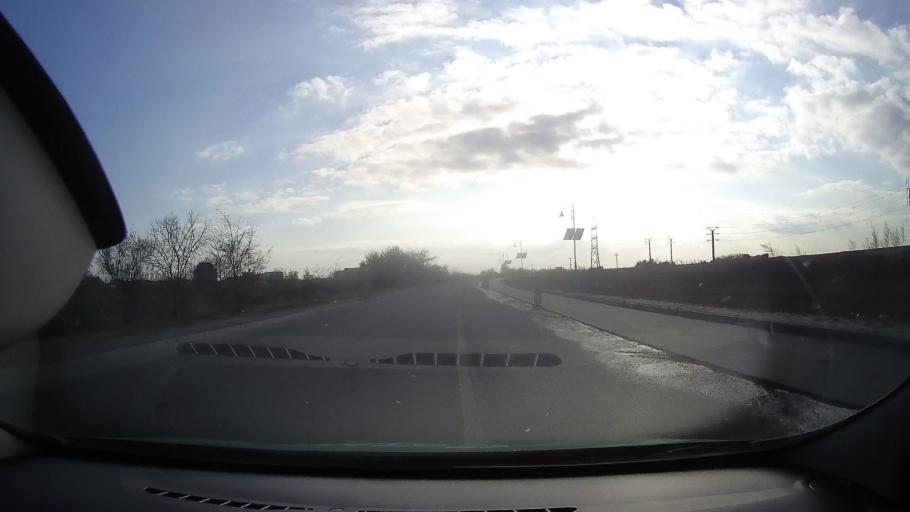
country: RO
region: Constanta
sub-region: Comuna Navodari
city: Navodari
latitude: 44.2943
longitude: 28.6128
